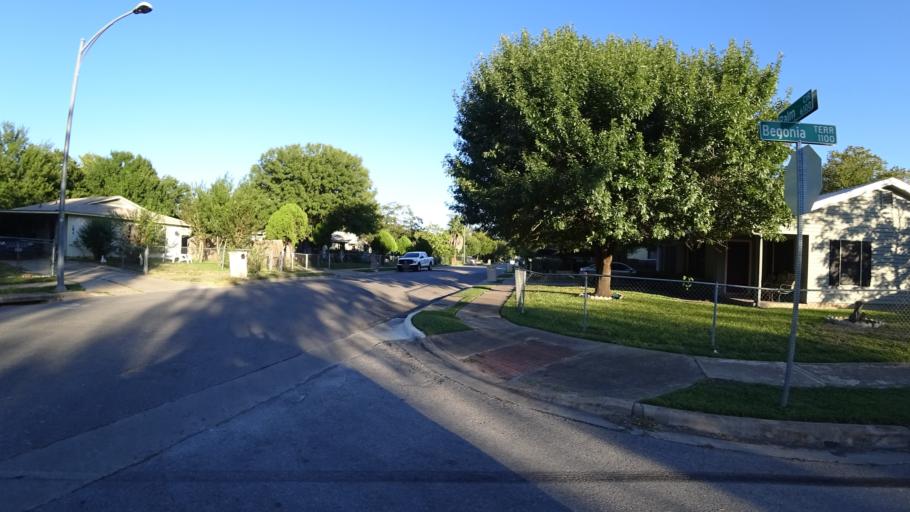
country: US
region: Texas
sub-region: Travis County
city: Austin
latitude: 30.2342
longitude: -97.7011
